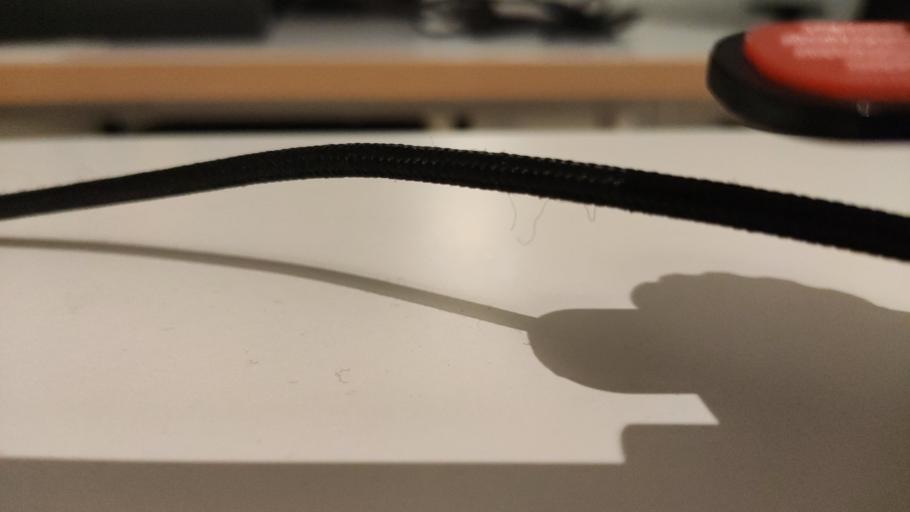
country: RU
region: Moskovskaya
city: Novosin'kovo
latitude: 56.3920
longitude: 37.2902
